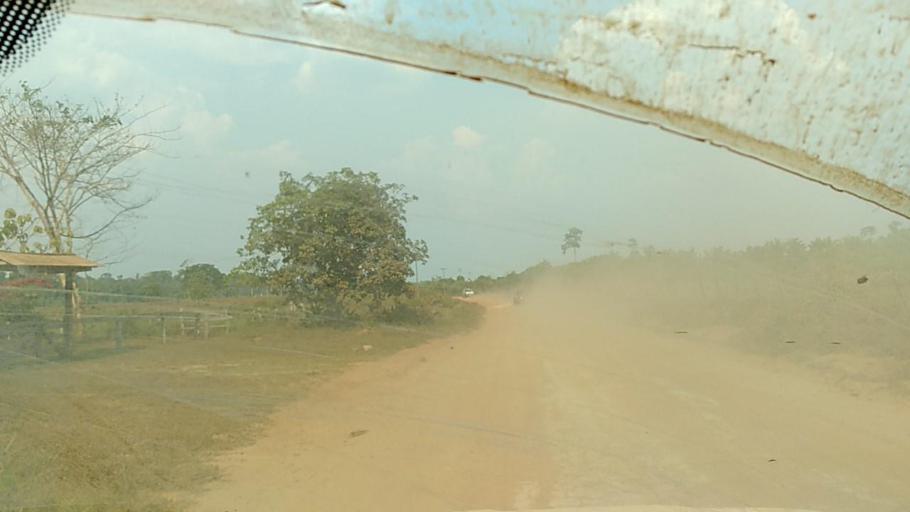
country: BR
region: Rondonia
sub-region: Porto Velho
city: Porto Velho
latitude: -8.6832
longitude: -63.2238
